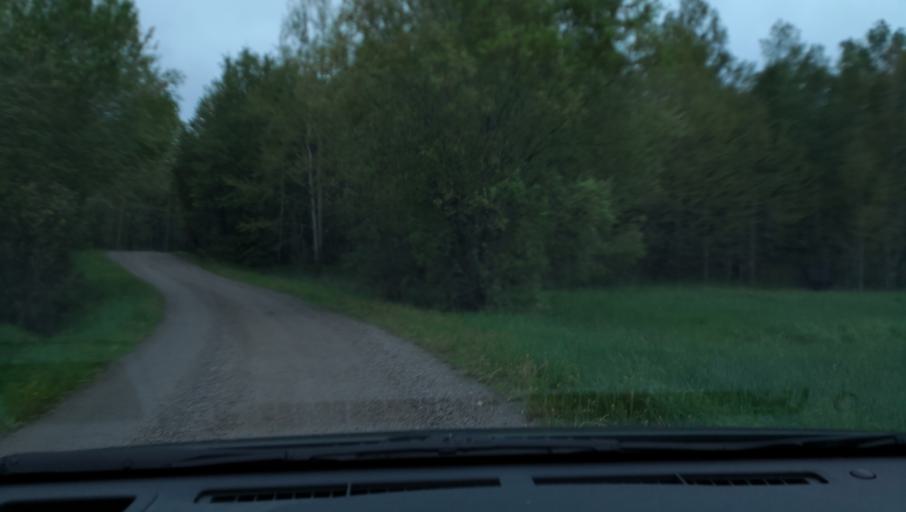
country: SE
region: Uppsala
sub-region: Heby Kommun
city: OEstervala
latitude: 59.9924
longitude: 17.2517
